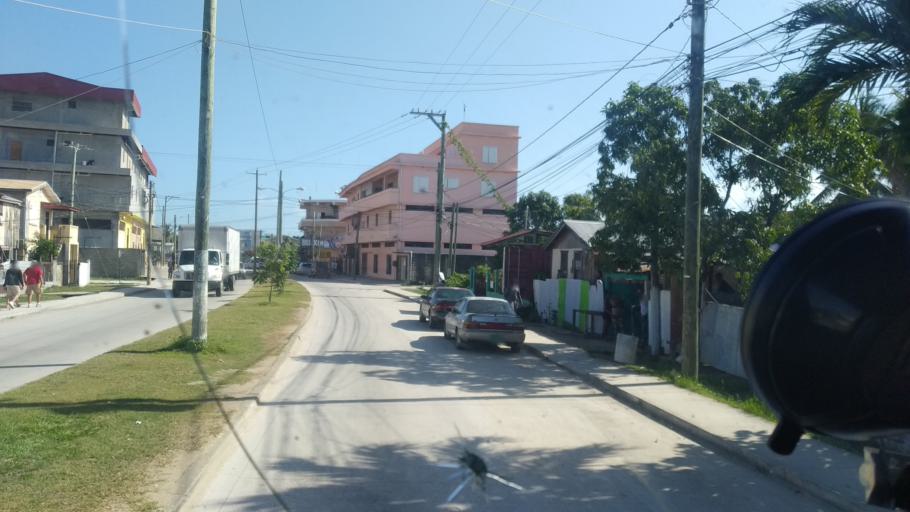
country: BZ
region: Belize
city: Belize City
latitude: 17.4895
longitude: -88.1997
